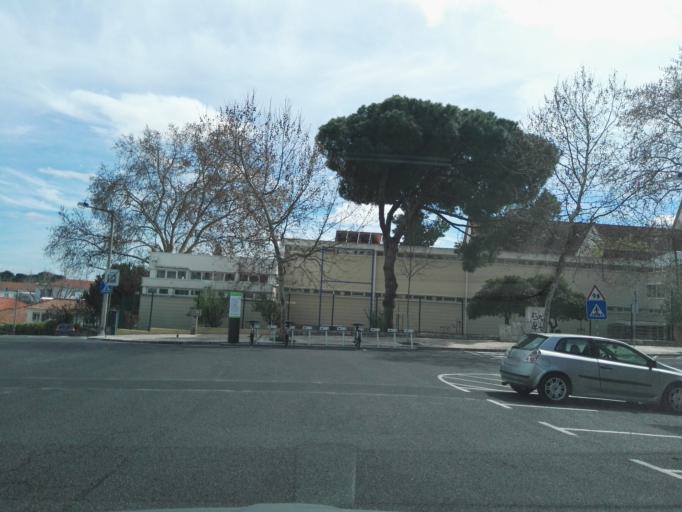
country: PT
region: Lisbon
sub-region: Lisbon
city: Lisbon
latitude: 38.7567
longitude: -9.1374
